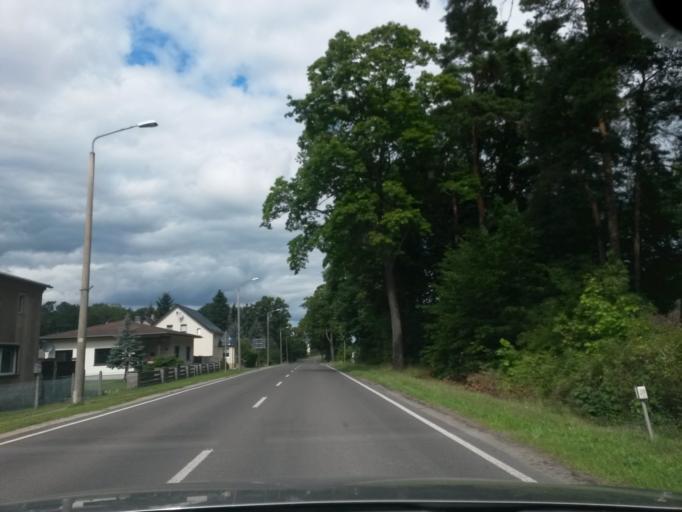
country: DE
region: Brandenburg
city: Chorin
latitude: 52.9305
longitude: 13.9208
